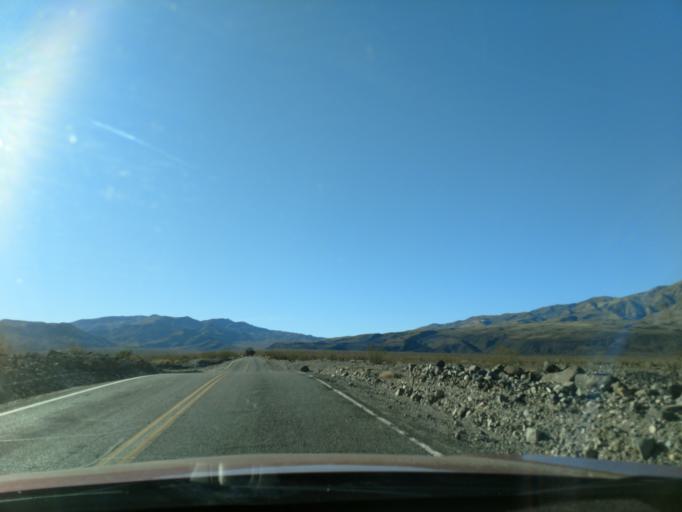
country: US
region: Nevada
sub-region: Nye County
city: Beatty
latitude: 36.5033
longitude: -117.2257
